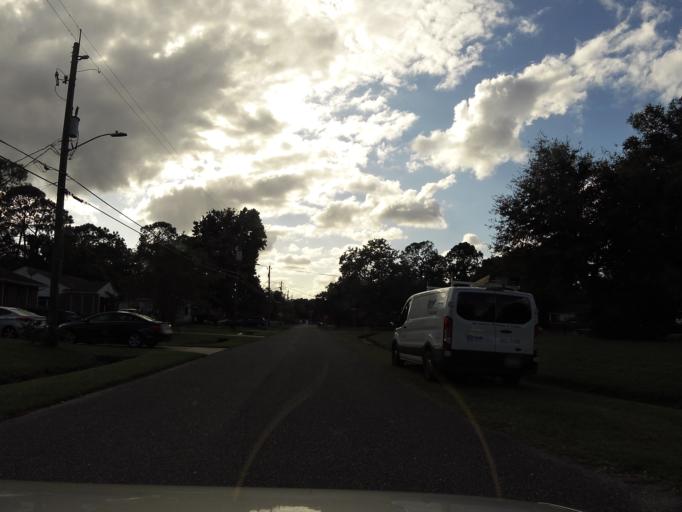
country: US
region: Florida
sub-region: Duval County
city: Jacksonville
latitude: 30.2868
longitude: -81.7278
